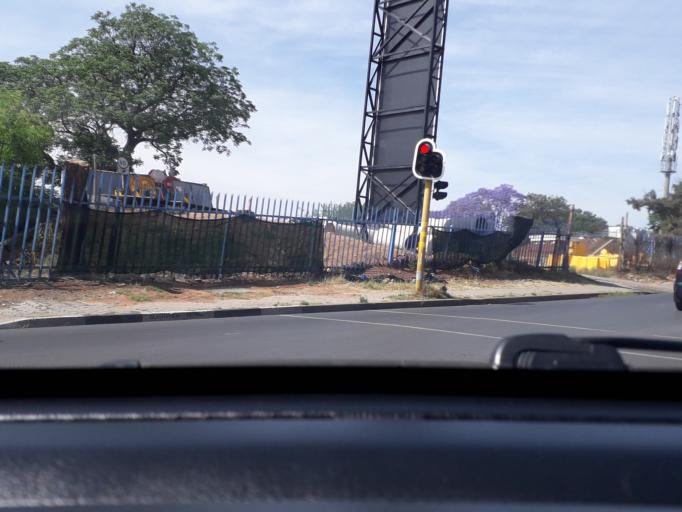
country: ZA
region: Gauteng
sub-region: City of Johannesburg Metropolitan Municipality
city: Johannesburg
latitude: -26.1351
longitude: 28.0933
